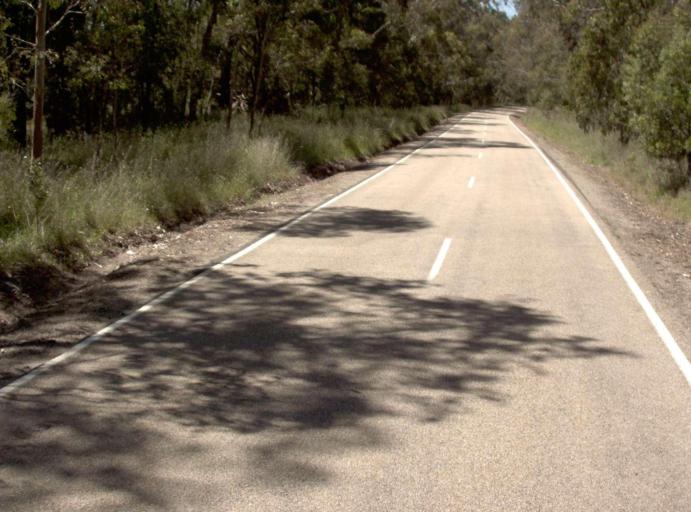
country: AU
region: Victoria
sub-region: East Gippsland
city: Lakes Entrance
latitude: -37.2620
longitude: 148.2487
